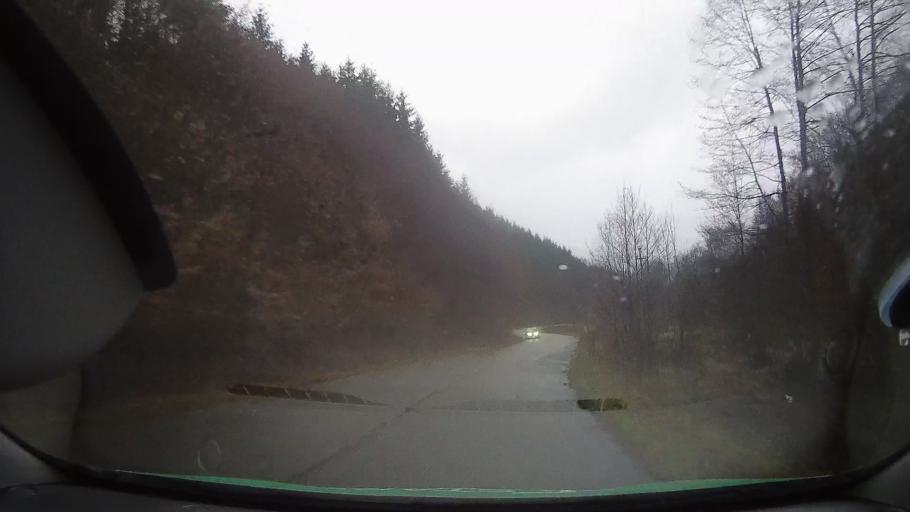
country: RO
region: Alba
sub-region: Comuna Avram Iancu
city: Avram Iancu
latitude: 46.2951
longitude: 22.7557
